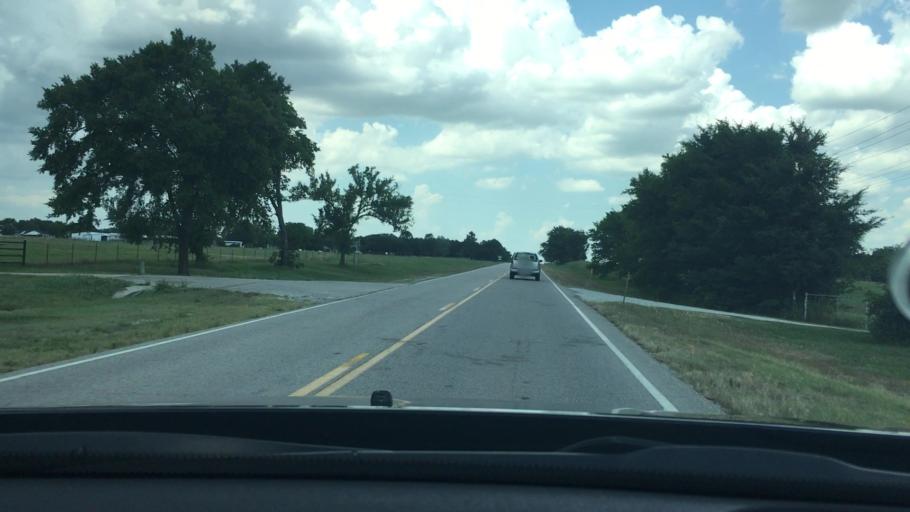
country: US
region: Oklahoma
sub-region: Pontotoc County
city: Ada
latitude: 34.6607
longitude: -96.6349
